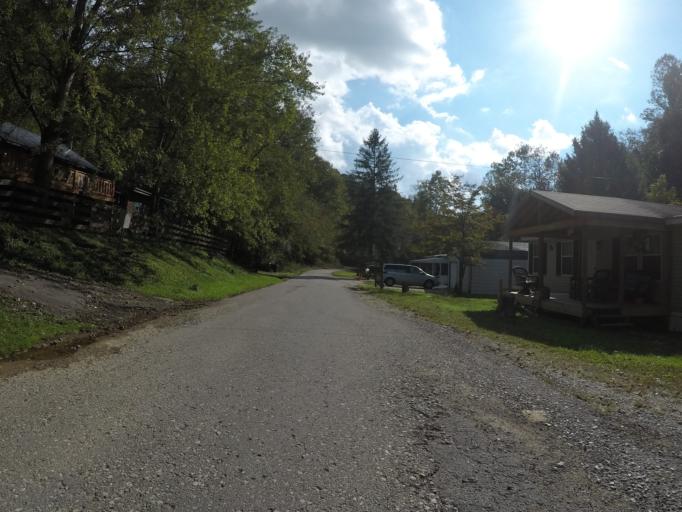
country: US
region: West Virginia
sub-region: Wayne County
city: Lavalette
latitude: 38.3561
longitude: -82.4893
